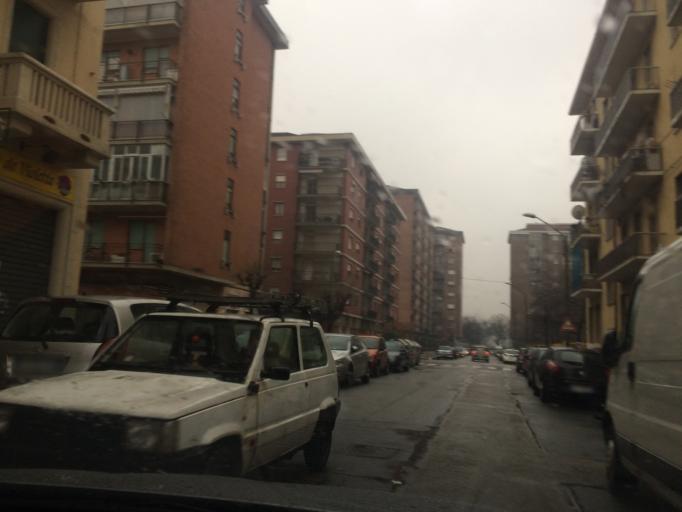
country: IT
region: Piedmont
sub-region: Provincia di Torino
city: Lesna
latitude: 45.0324
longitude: 7.6547
